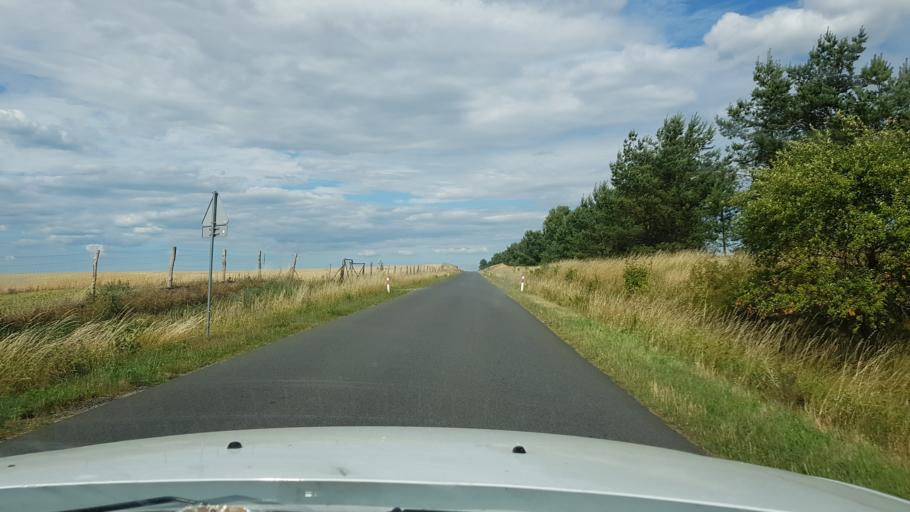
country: PL
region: West Pomeranian Voivodeship
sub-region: Powiat drawski
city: Wierzchowo
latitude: 53.4240
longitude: 16.0477
